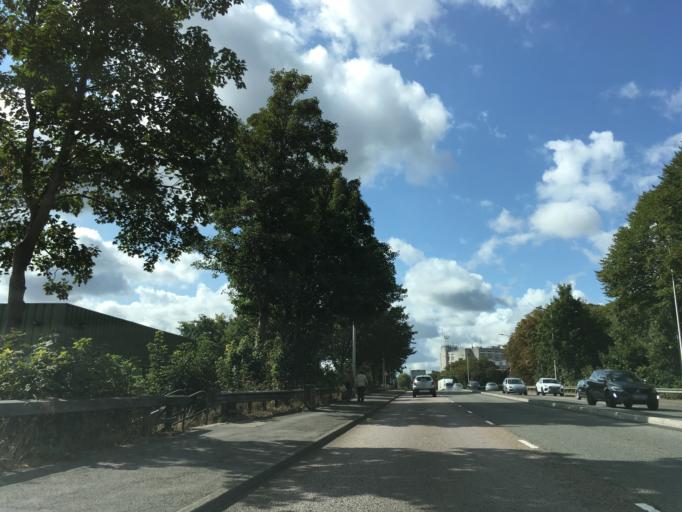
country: GB
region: England
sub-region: West Berkshire
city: Newbury
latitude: 51.4032
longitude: -1.3190
